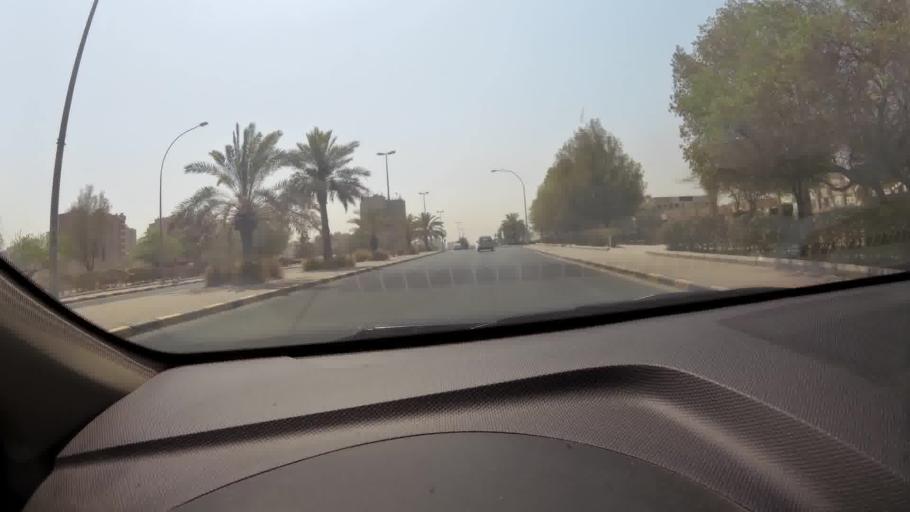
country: KW
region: Al Farwaniyah
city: Al Farwaniyah
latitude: 29.2594
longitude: 47.9454
